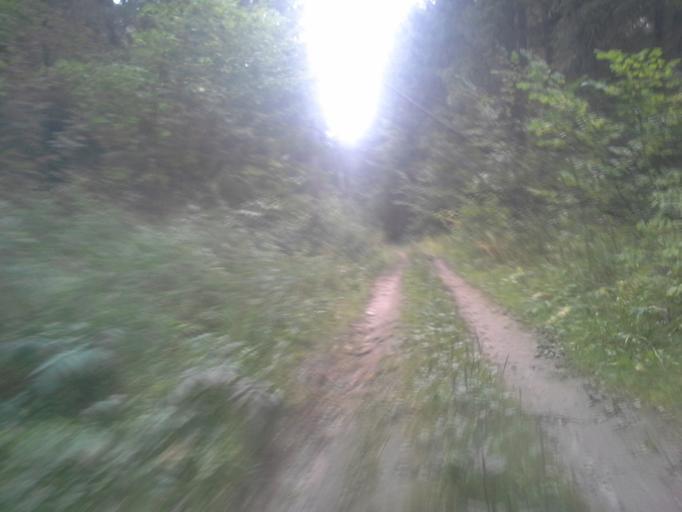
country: RU
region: Moskovskaya
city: Selyatino
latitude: 55.4554
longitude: 36.9764
